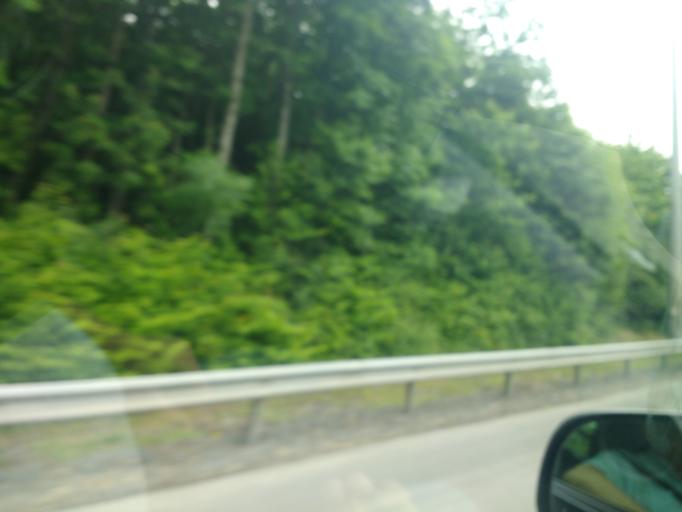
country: IE
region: Leinster
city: Kinsealy-Drinan
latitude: 53.4448
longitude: -6.2051
